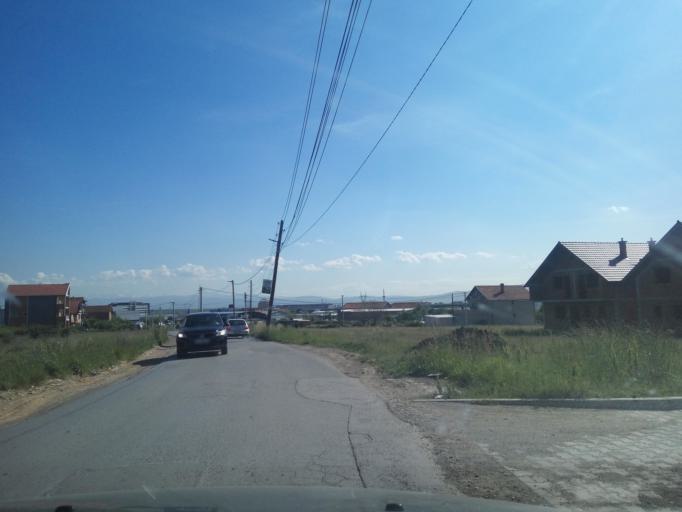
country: XK
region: Pristina
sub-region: Kosovo Polje
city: Kosovo Polje
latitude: 42.6541
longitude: 21.1268
